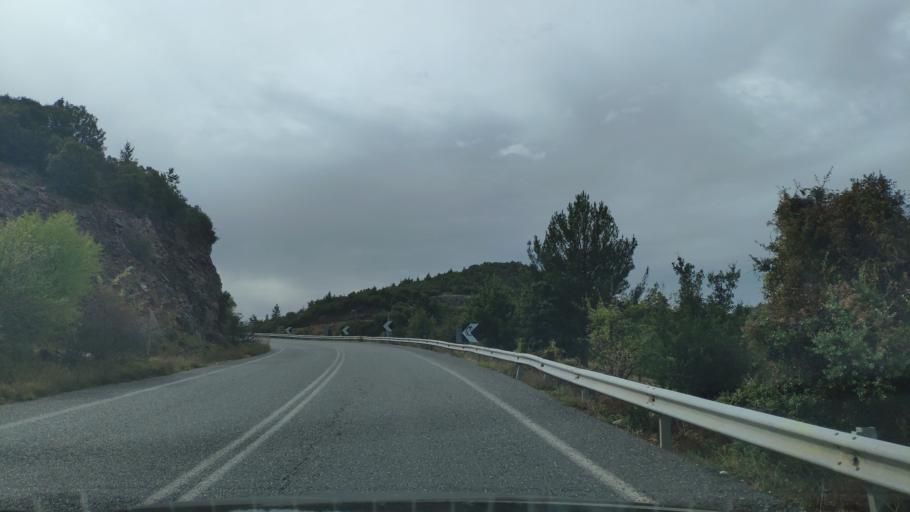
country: GR
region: Peloponnese
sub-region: Nomos Arkadias
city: Langadhia
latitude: 37.6847
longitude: 22.1913
